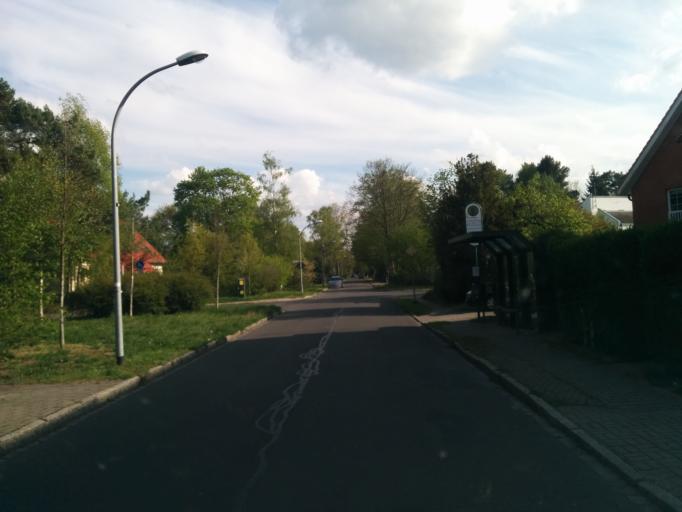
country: DE
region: Brandenburg
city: Kleinmachnow
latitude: 52.4049
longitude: 13.2056
